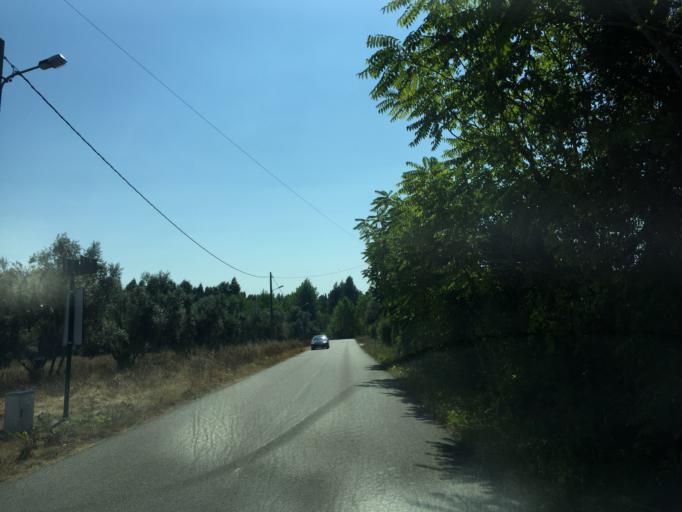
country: PT
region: Coimbra
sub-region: Cantanhede
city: Cantanhede
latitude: 40.3368
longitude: -8.6075
